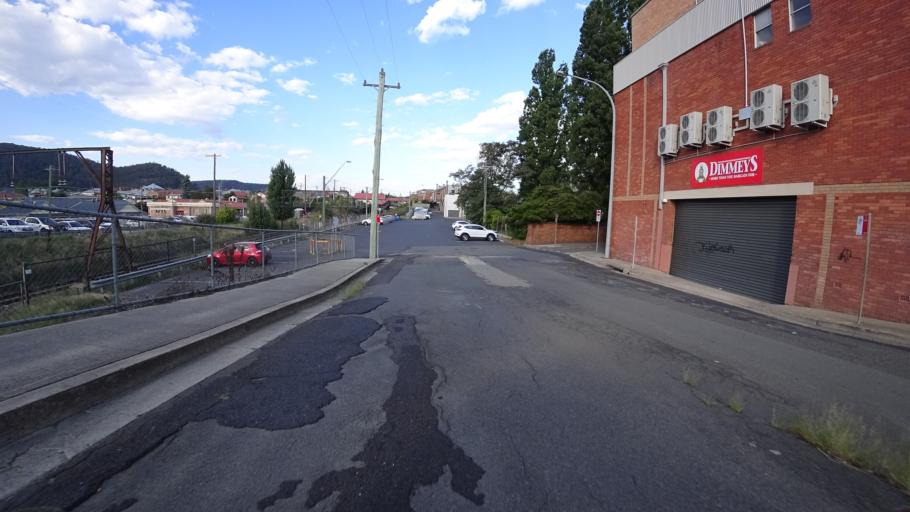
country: AU
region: New South Wales
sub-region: Lithgow
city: Lithgow
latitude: -33.4814
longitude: 150.1545
